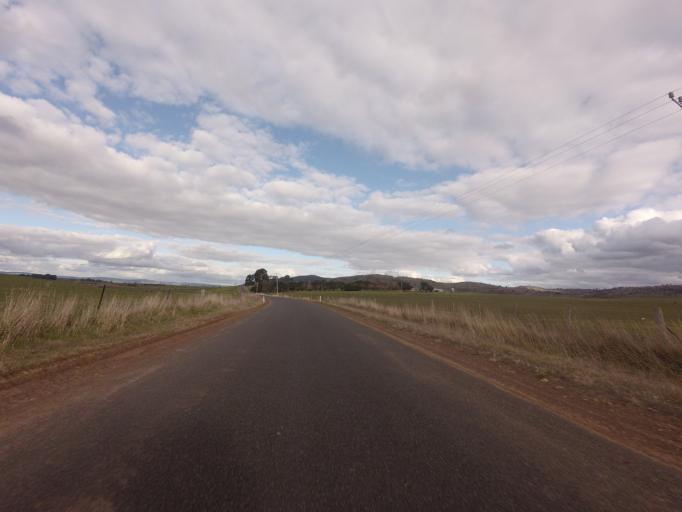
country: AU
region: Tasmania
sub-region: Northern Midlands
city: Evandale
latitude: -41.9022
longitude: 147.3521
